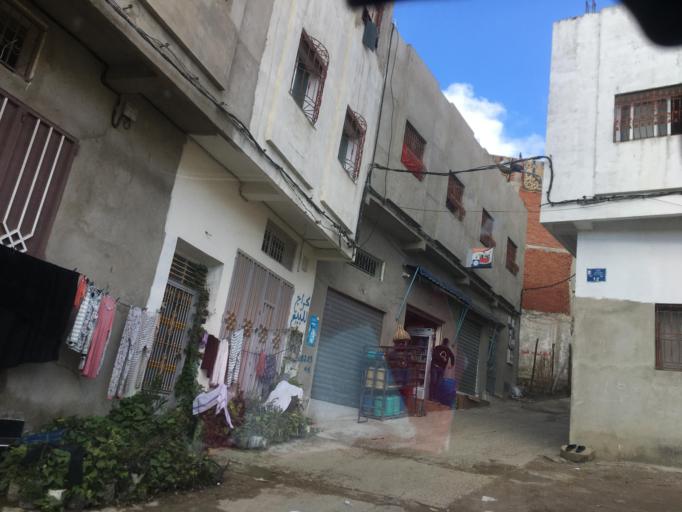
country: MA
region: Tanger-Tetouan
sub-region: Tanger-Assilah
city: Tangier
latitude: 35.7149
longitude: -5.8090
